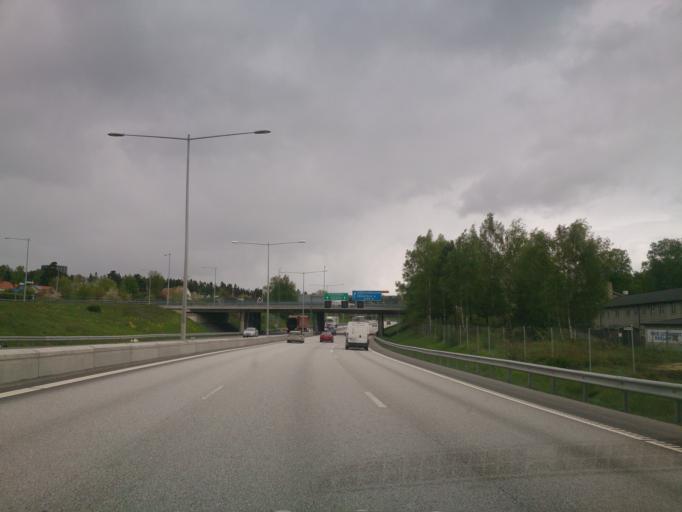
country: SE
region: Stockholm
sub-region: Sodertalje Kommun
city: Soedertaelje
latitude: 59.1883
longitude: 17.6462
